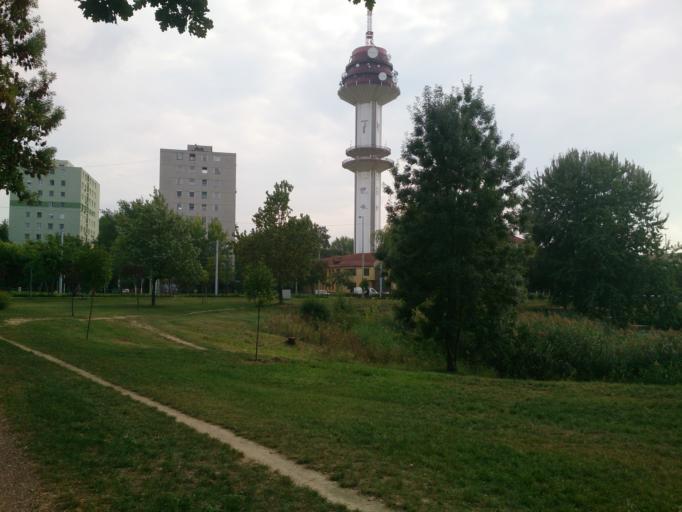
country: HU
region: Csongrad
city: Szeged
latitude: 46.2732
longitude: 20.1463
